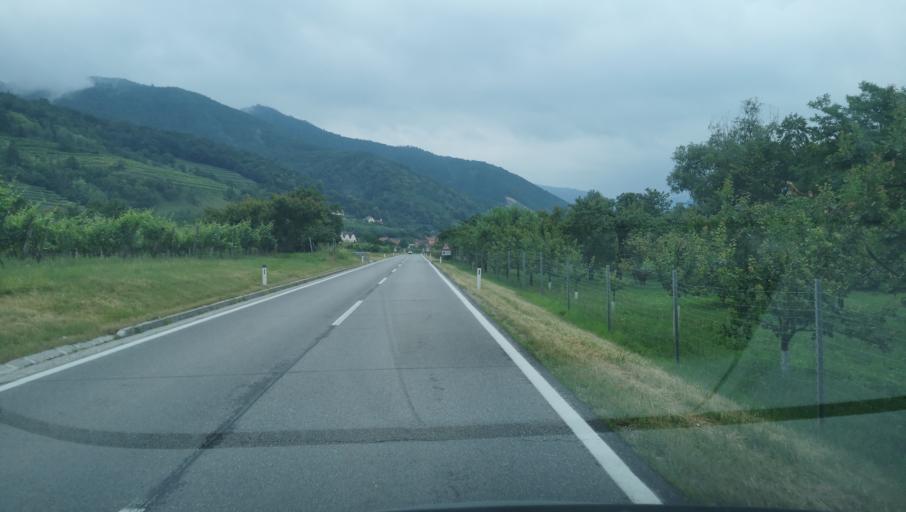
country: AT
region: Lower Austria
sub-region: Politischer Bezirk Krems
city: Spitz
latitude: 48.3322
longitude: 15.4054
